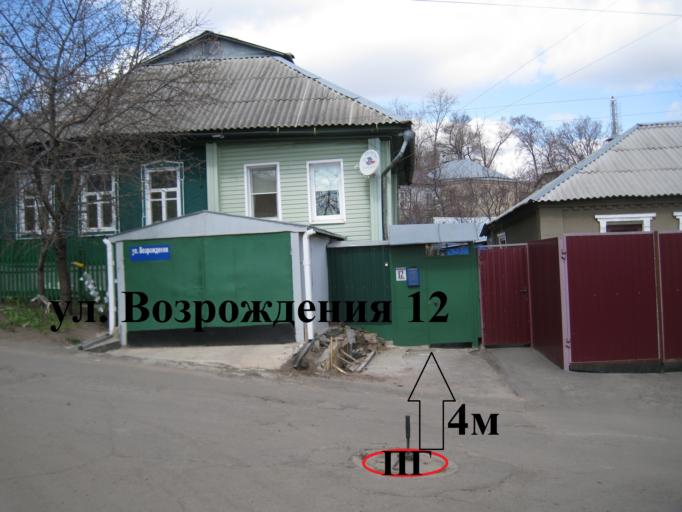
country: RU
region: Voronezj
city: Voronezh
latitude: 51.6317
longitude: 39.1915
